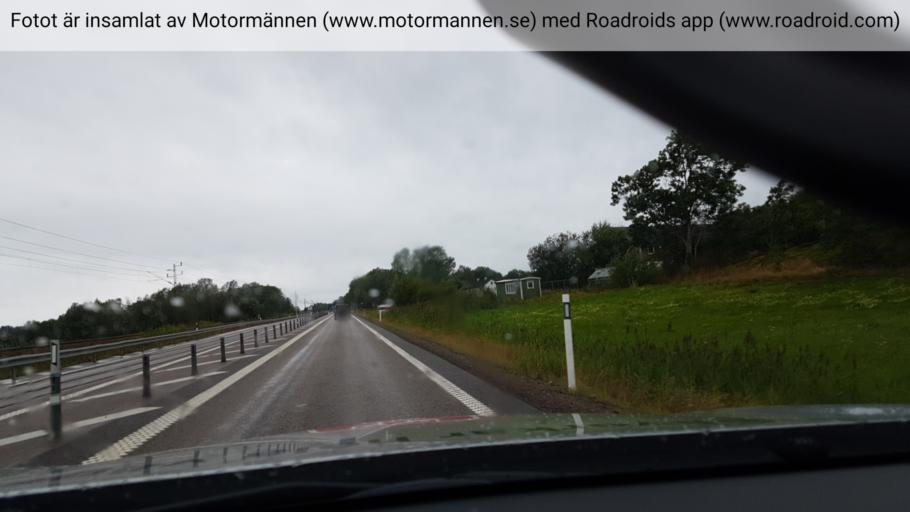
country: SE
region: Vaestra Goetaland
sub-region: Melleruds Kommun
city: Mellerud
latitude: 58.8541
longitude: 12.5577
